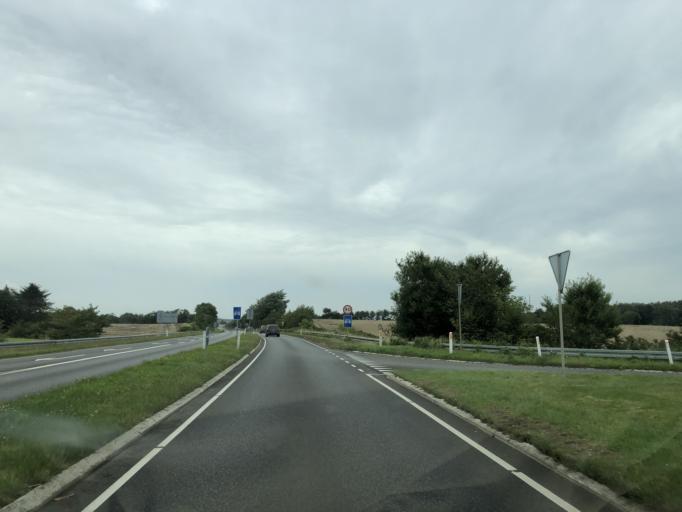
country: DK
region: North Denmark
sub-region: Morso Kommune
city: Nykobing Mors
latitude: 56.7675
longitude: 8.8308
